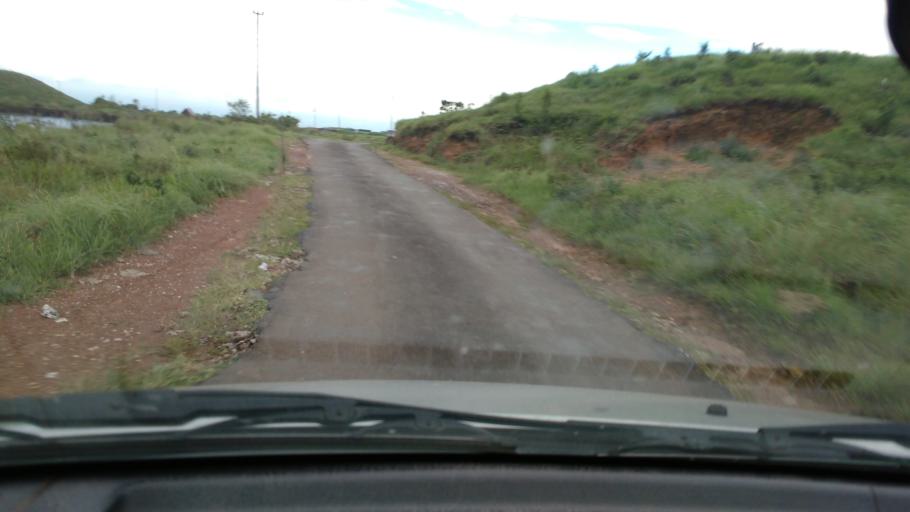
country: IN
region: Meghalaya
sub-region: East Khasi Hills
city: Cherrapunji
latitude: 25.2769
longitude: 91.6919
